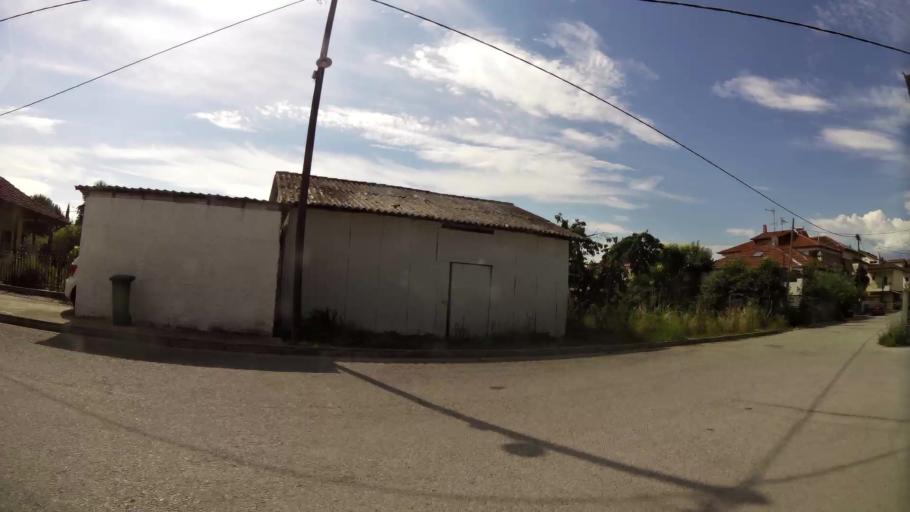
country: GR
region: Central Macedonia
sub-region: Nomos Pierias
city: Katerini
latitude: 40.2817
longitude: 22.5060
